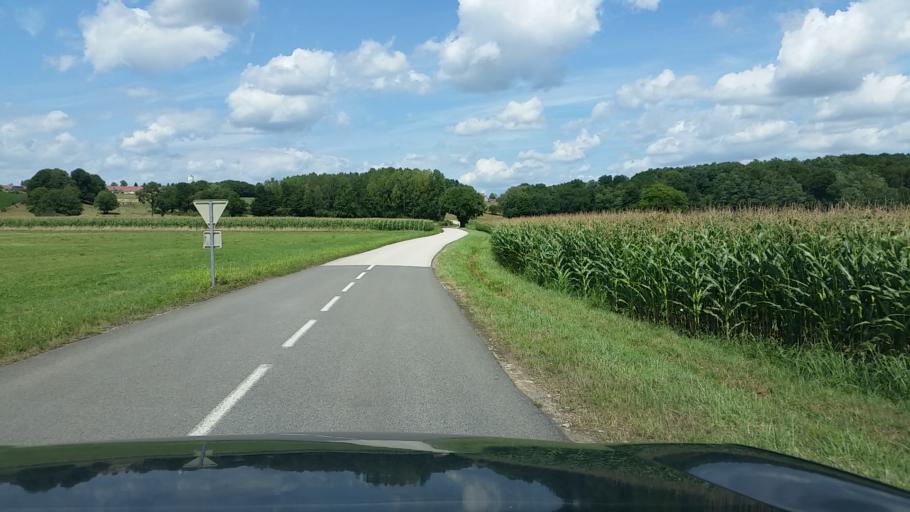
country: FR
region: Franche-Comte
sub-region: Departement du Jura
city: Bletterans
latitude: 46.7736
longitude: 5.5042
